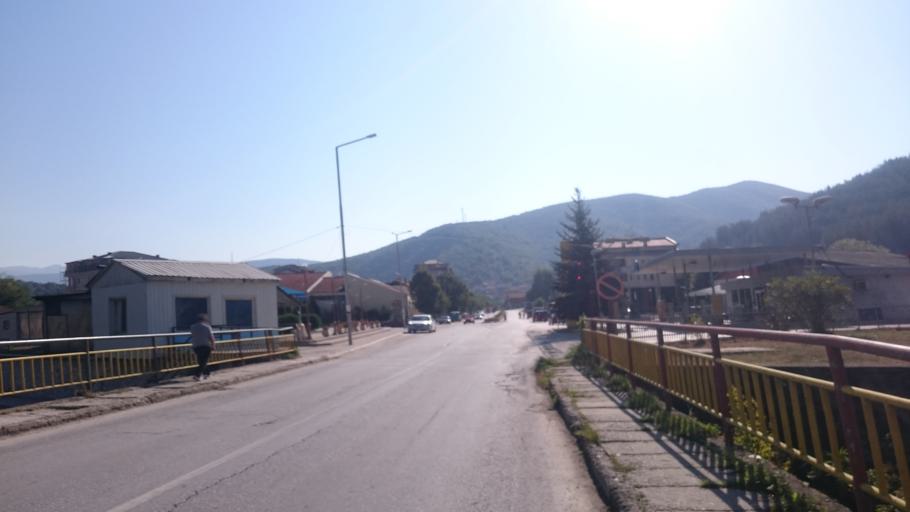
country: MK
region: Makedonski Brod
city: Makedonski Brod
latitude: 41.5073
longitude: 21.2160
